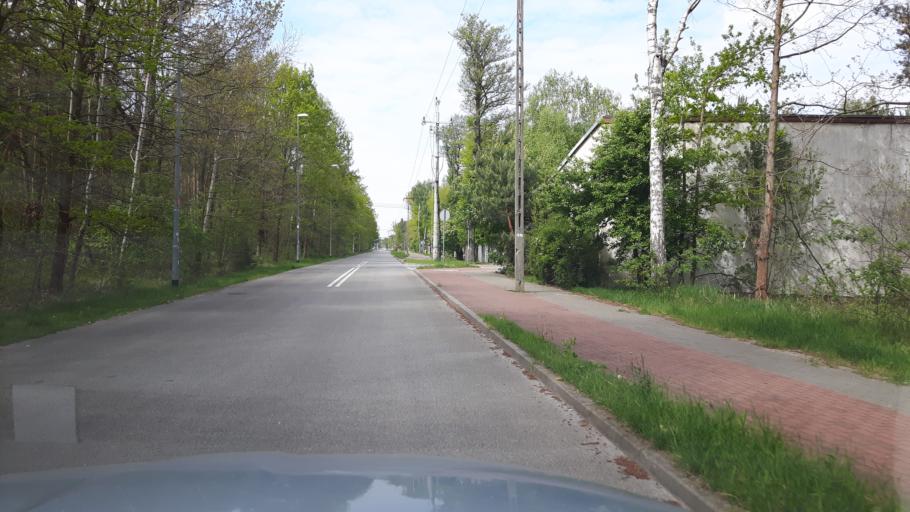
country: PL
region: Masovian Voivodeship
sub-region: Warszawa
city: Wesola
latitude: 52.2497
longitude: 21.2016
